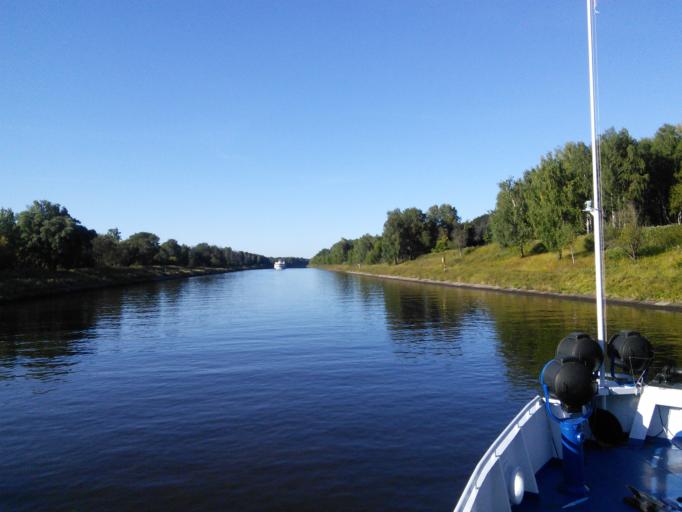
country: RU
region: Moskovskaya
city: Yakhroma
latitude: 56.3025
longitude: 37.4892
